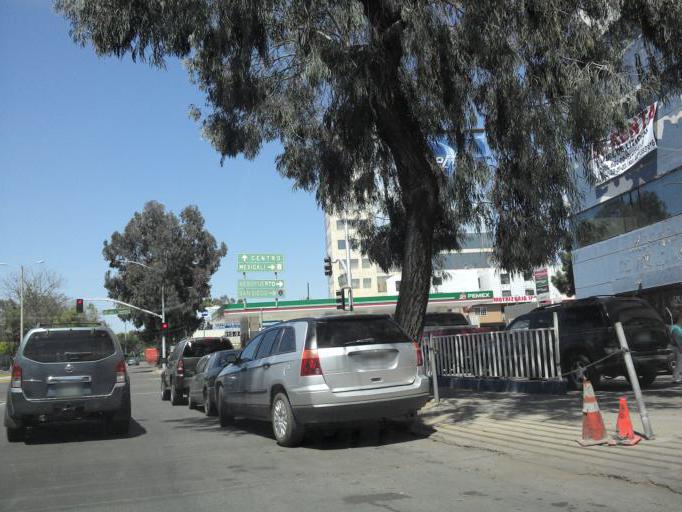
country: MX
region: Baja California
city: Tijuana
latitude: 32.5186
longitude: -117.0115
